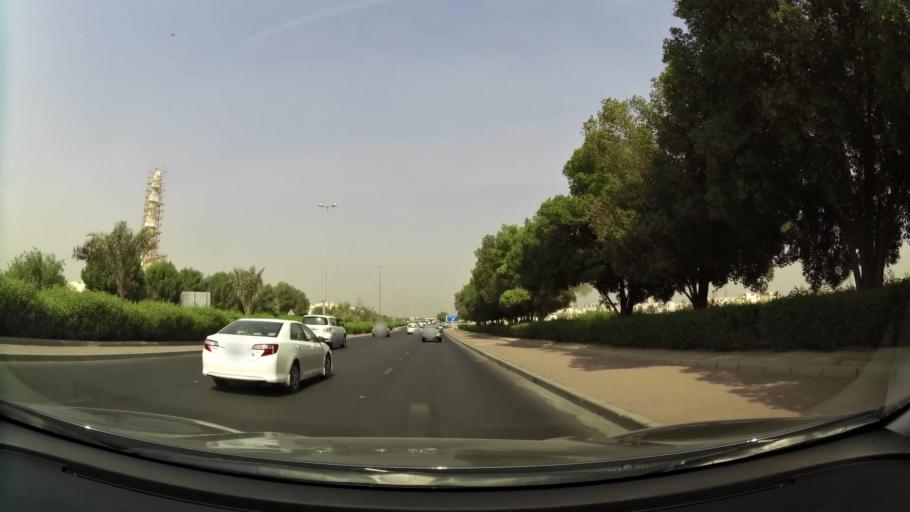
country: KW
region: Al Asimah
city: Ar Rabiyah
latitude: 29.2906
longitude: 47.9061
